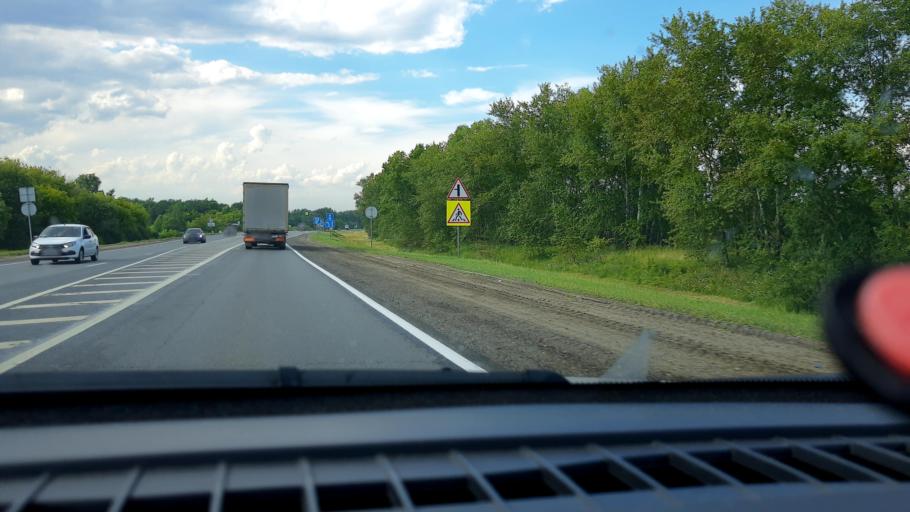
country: RU
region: Nizjnij Novgorod
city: Pamyat' Parizhskoy Kommuny
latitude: 56.0115
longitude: 44.6267
